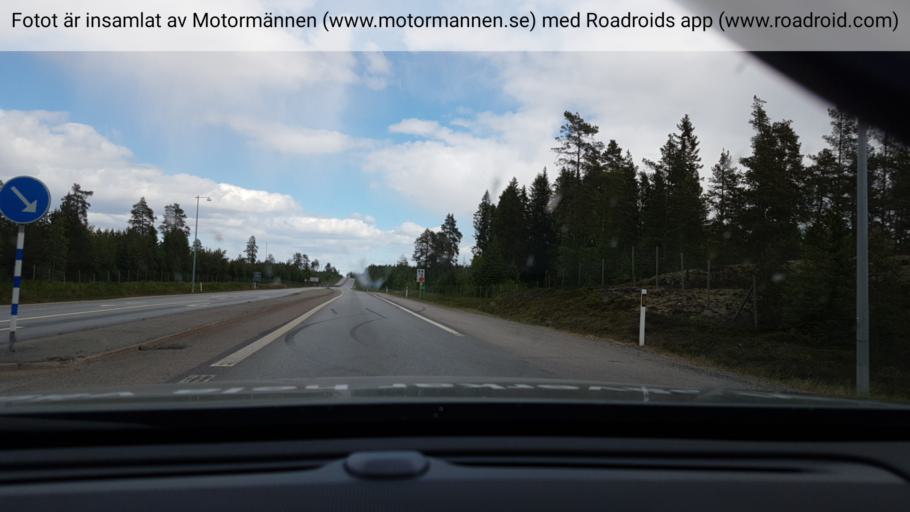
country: SE
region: Vaesterbotten
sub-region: Umea Kommun
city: Hoernefors
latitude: 63.6410
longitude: 19.9233
